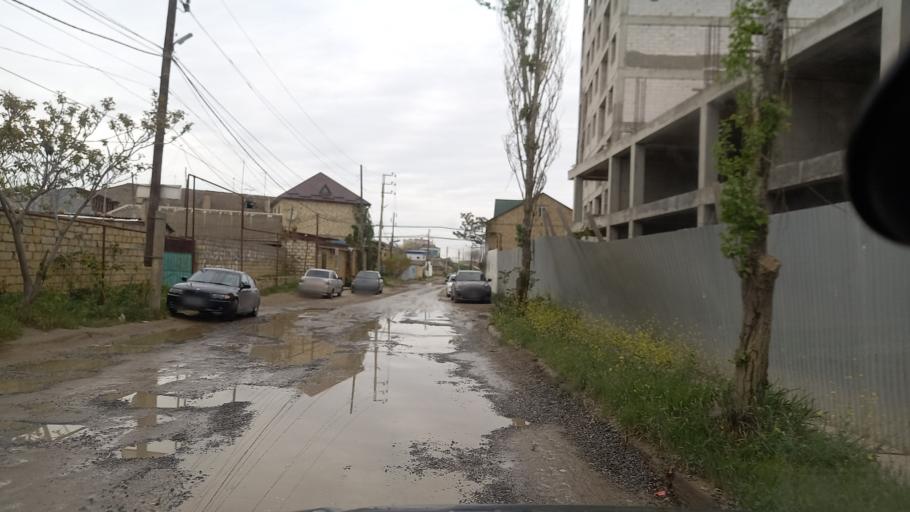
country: RU
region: Dagestan
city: Derbent
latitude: 42.0694
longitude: 48.3008
